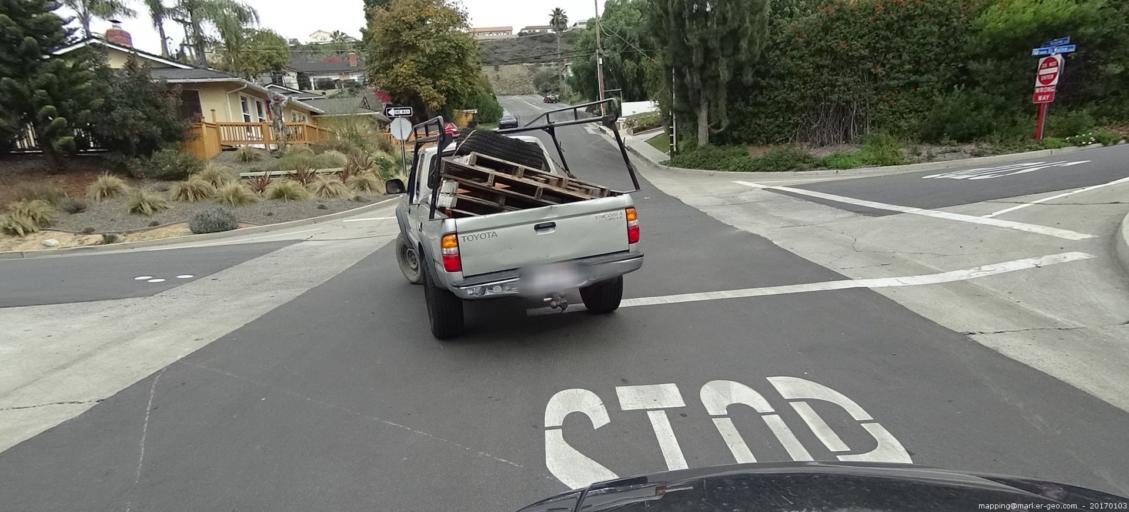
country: US
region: California
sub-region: Orange County
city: Dana Point
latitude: 33.4648
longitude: -117.6619
